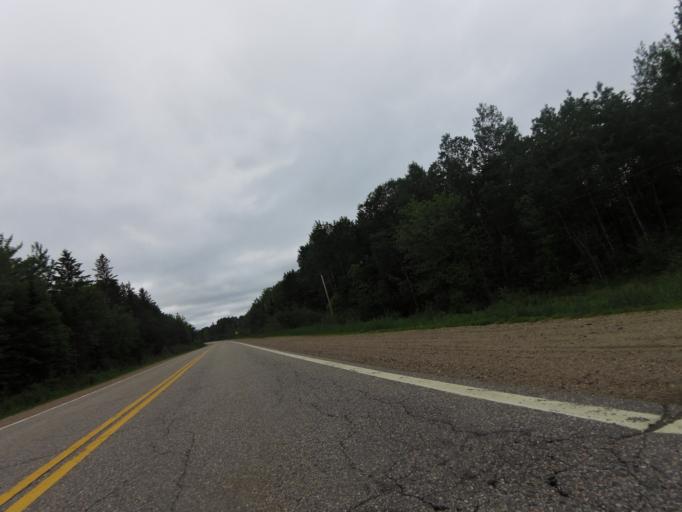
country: CA
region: Quebec
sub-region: Outaouais
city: Shawville
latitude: 45.8751
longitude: -76.4018
